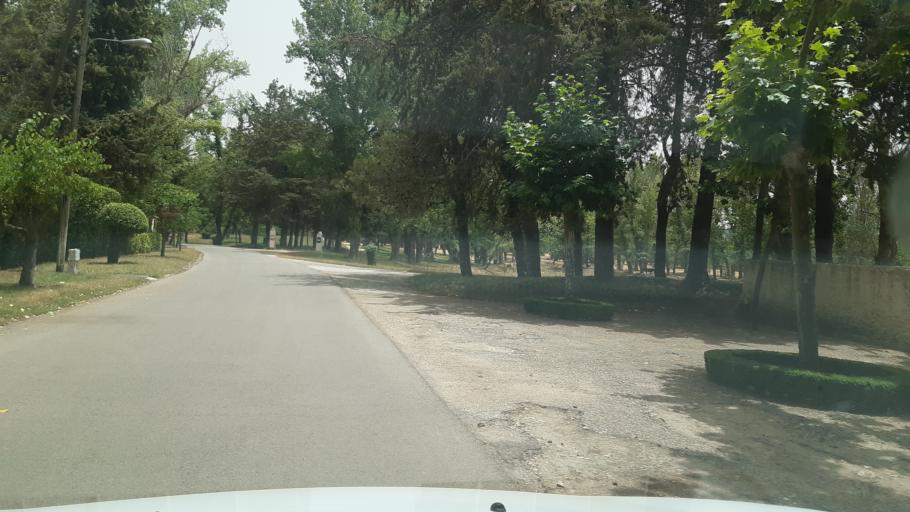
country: MA
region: Meknes-Tafilalet
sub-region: Ifrane
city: Ifrane
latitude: 33.6479
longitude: -5.0330
